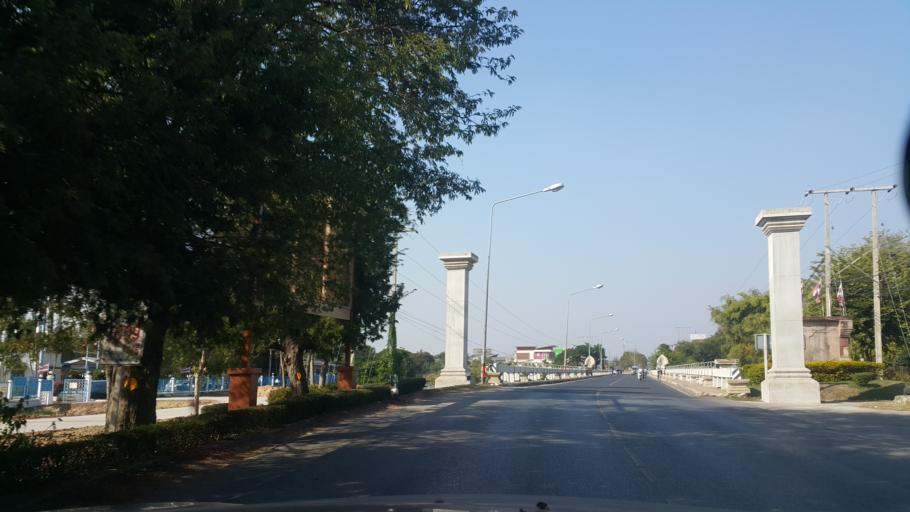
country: TH
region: Nakhon Ratchasima
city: Phimai
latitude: 15.2244
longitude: 102.4940
